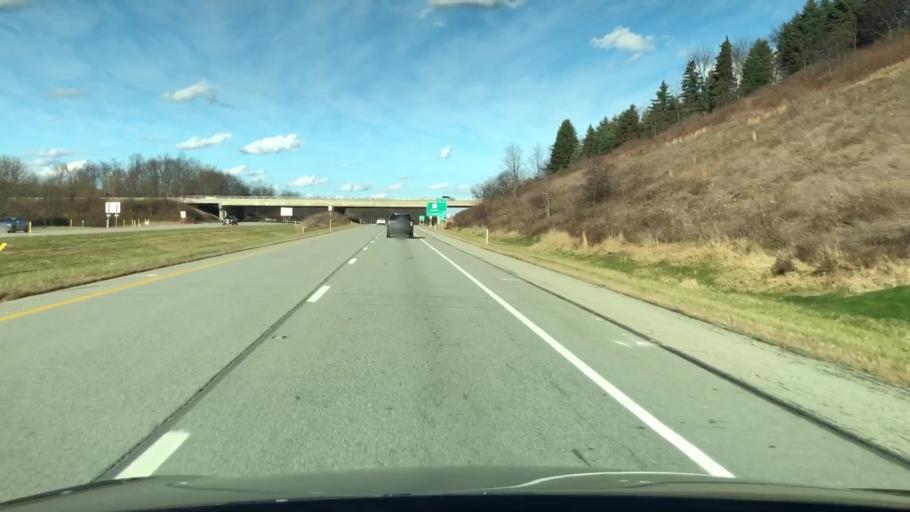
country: US
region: Pennsylvania
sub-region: Armstrong County
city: Freeport
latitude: 40.6890
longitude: -79.7131
